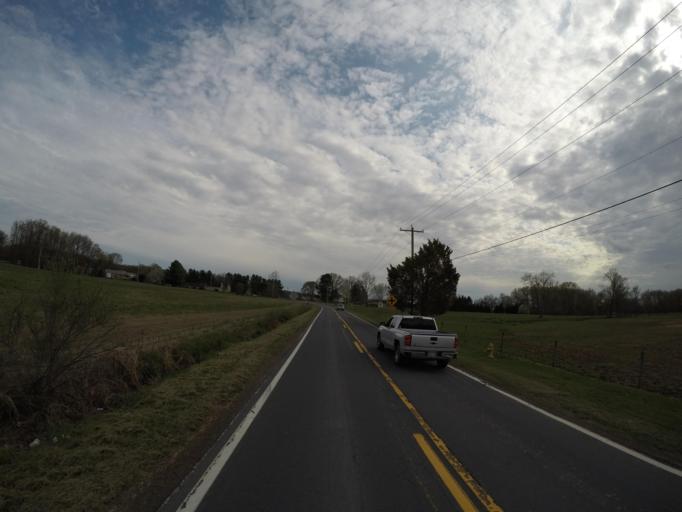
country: US
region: Delaware
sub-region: New Castle County
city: Glasgow
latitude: 39.5633
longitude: -75.7632
